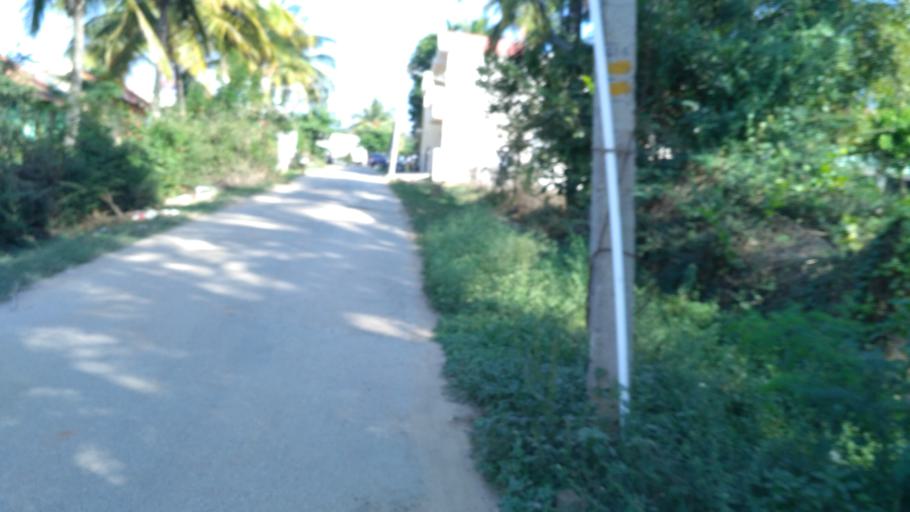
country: IN
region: Karnataka
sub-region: Hassan
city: Hassan
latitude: 13.0010
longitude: 76.1216
